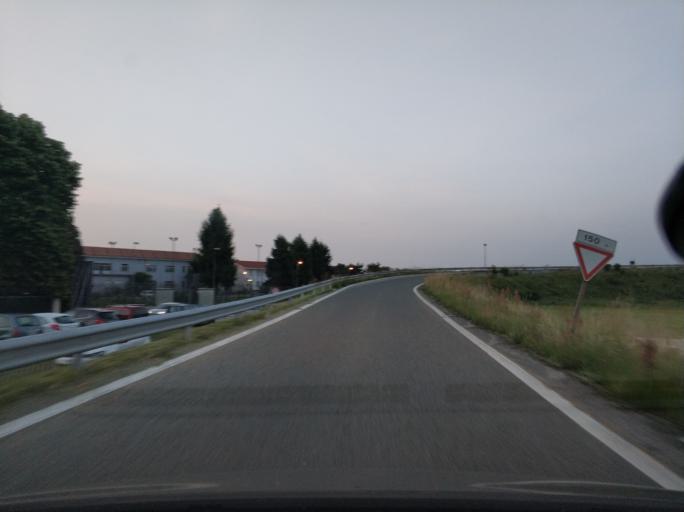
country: IT
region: Piedmont
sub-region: Provincia di Torino
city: Caselle Torinese
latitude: 45.1883
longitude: 7.6433
